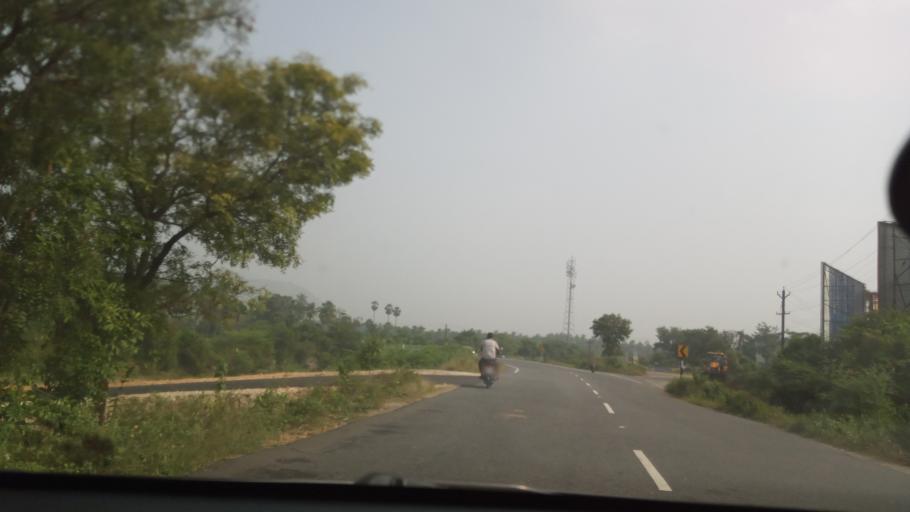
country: IN
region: Tamil Nadu
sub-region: Erode
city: Punjai Puliyampatti
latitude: 11.3198
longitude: 77.1479
